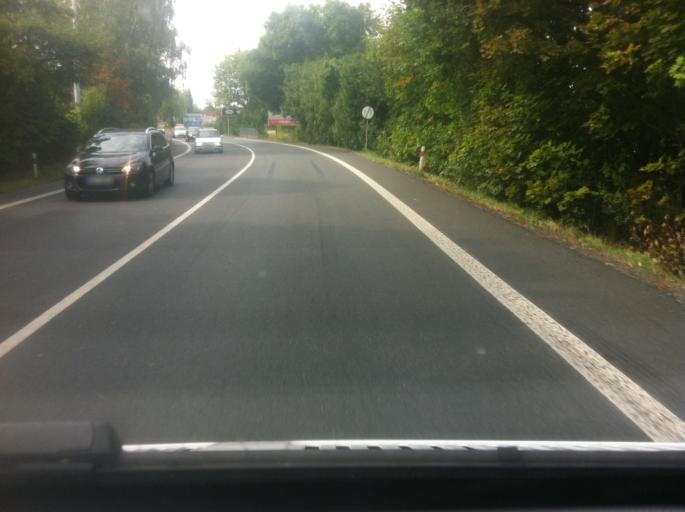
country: CZ
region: Zlin
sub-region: Okres Zlin
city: Zlin
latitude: 49.2245
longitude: 17.6977
